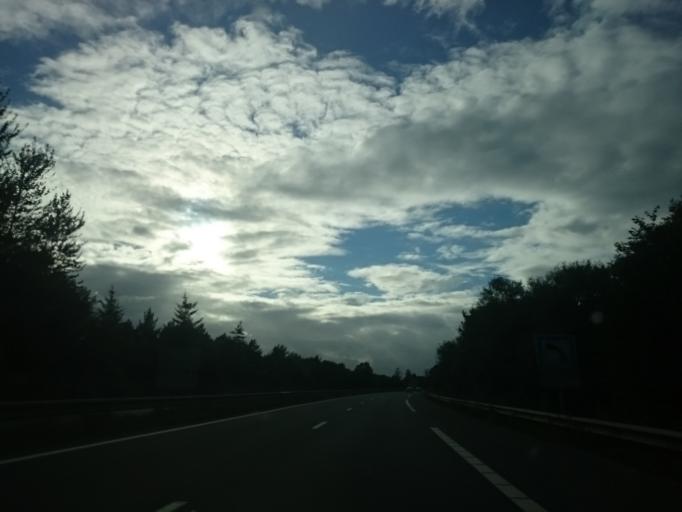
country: FR
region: Brittany
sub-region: Departement des Cotes-d'Armor
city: Plounevez-Moedec
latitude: 48.5623
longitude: -3.5162
